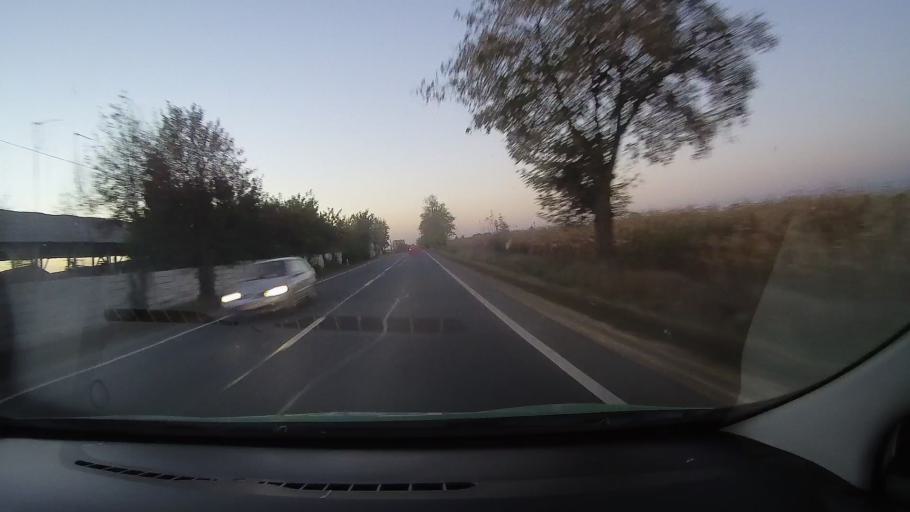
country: RO
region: Bihor
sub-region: Comuna Valea lui Mihai
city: Valea lui Mihai
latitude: 47.5000
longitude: 22.1484
